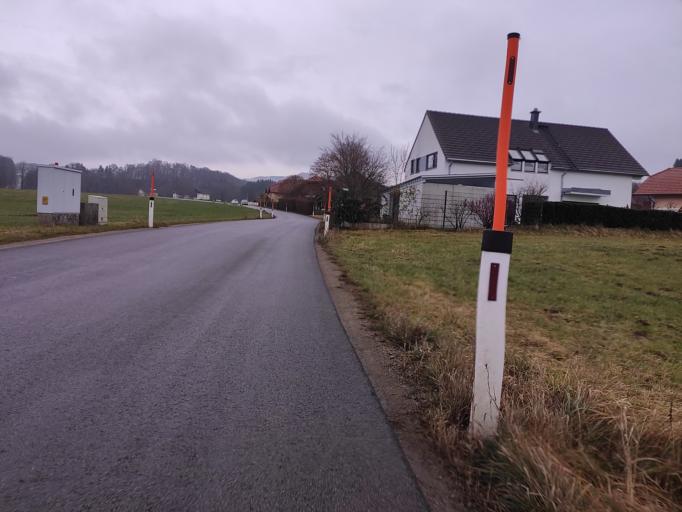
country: AT
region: Salzburg
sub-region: Politischer Bezirk Salzburg-Umgebung
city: Henndorf am Wallersee
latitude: 47.8960
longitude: 13.1589
